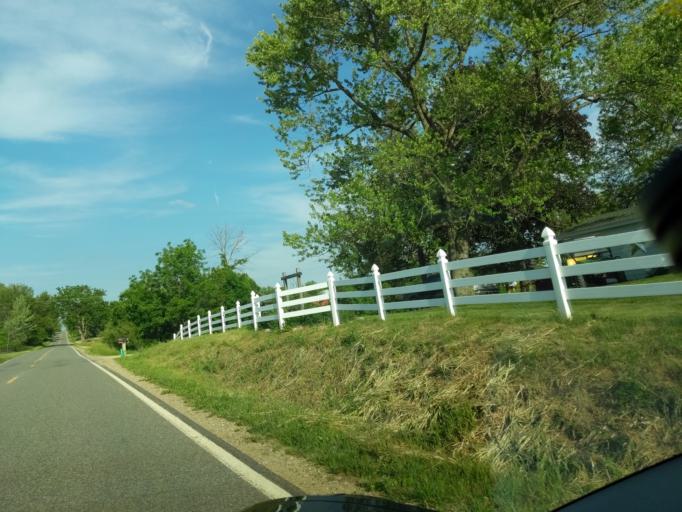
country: US
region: Michigan
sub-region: Barry County
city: Nashville
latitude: 42.6250
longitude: -85.1250
